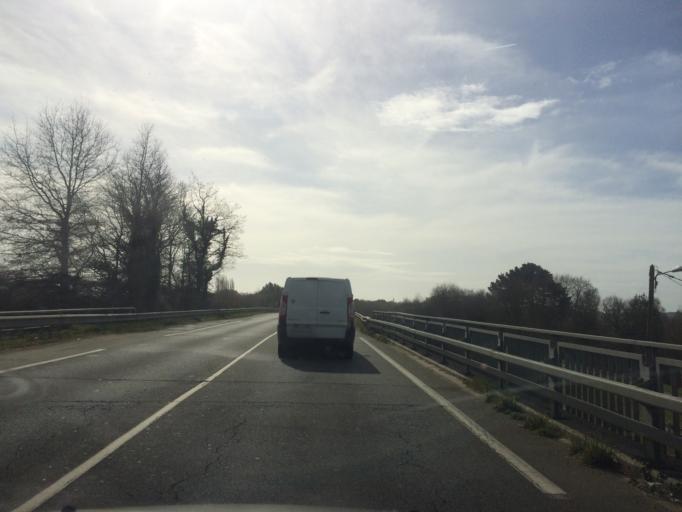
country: FR
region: Pays de la Loire
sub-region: Departement de la Loire-Atlantique
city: Saint-Nazaire
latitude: 47.2789
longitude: -2.2486
